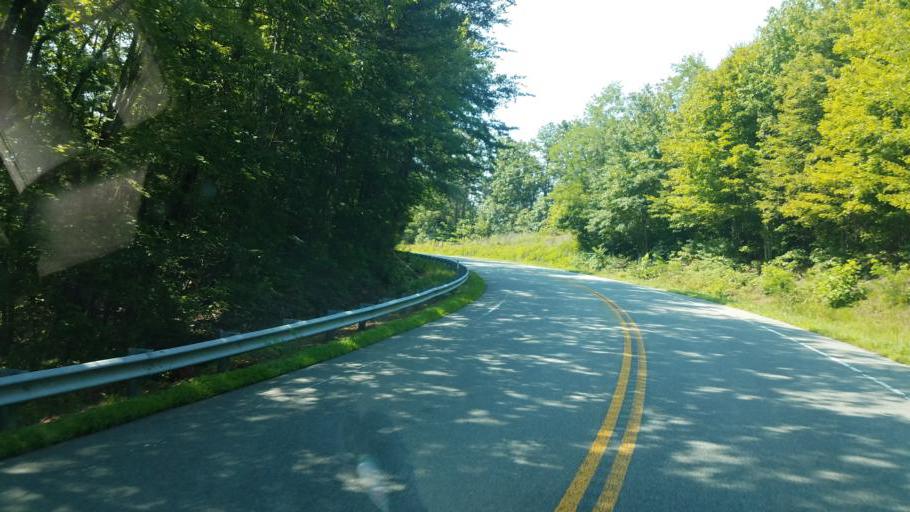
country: US
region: North Carolina
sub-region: Burke County
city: Glen Alpine
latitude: 35.9054
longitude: -81.8081
